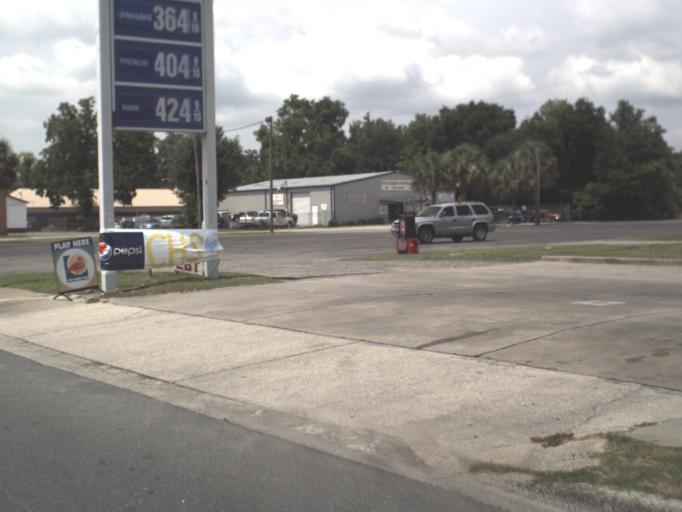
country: US
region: Florida
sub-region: Levy County
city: Chiefland
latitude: 29.4802
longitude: -82.8597
